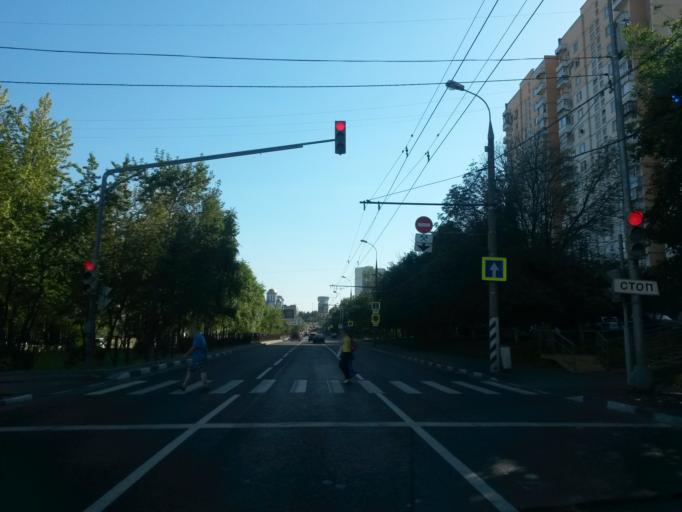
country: RU
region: Moscow
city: Yasenevo
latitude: 55.6195
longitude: 37.5421
